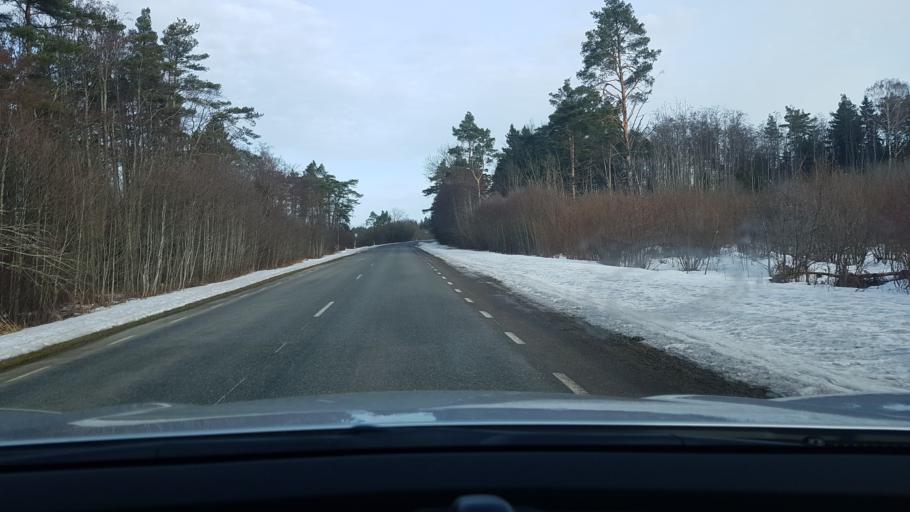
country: EE
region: Saare
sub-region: Kuressaare linn
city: Kuressaare
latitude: 58.4010
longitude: 22.6428
